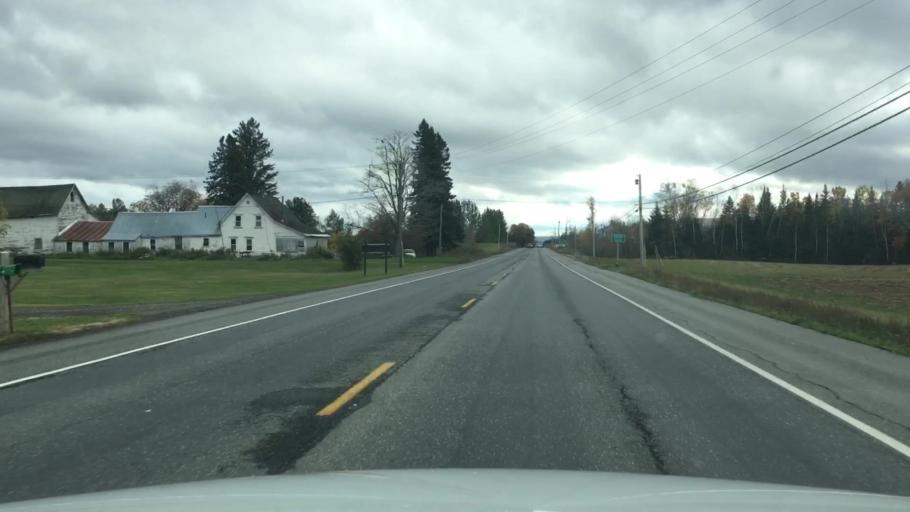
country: US
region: Maine
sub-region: Aroostook County
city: Houlton
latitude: 46.1860
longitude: -67.8412
